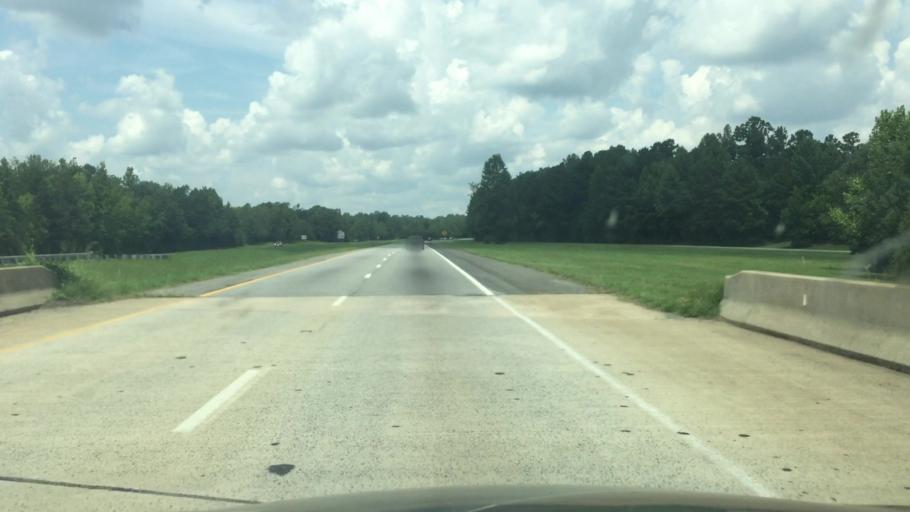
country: US
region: North Carolina
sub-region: Guilford County
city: Pleasant Garden
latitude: 35.9227
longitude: -79.8253
